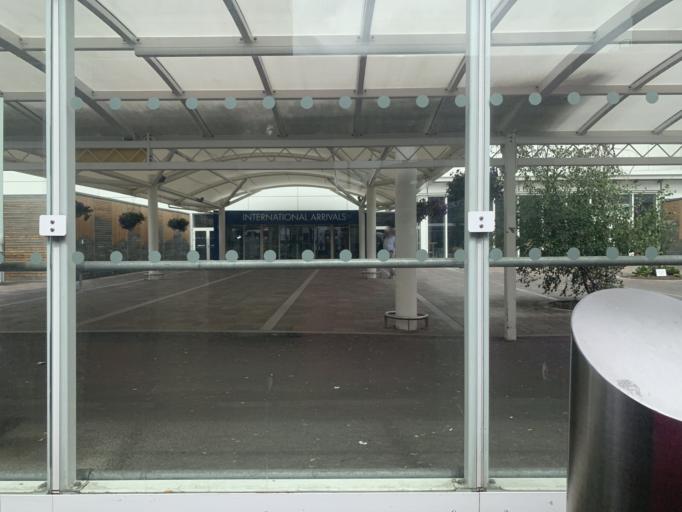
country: GB
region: Scotland
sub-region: Renfrewshire
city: Inchinnan
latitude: 55.8641
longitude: -4.4330
